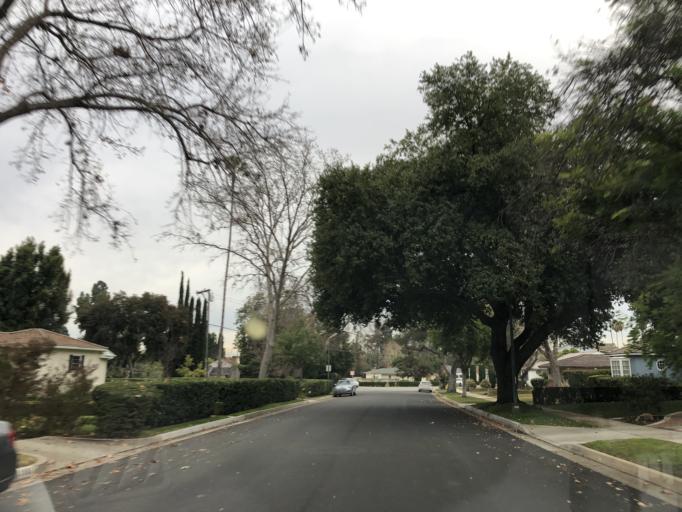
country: US
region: California
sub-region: Los Angeles County
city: San Marino
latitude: 34.1159
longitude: -118.0985
